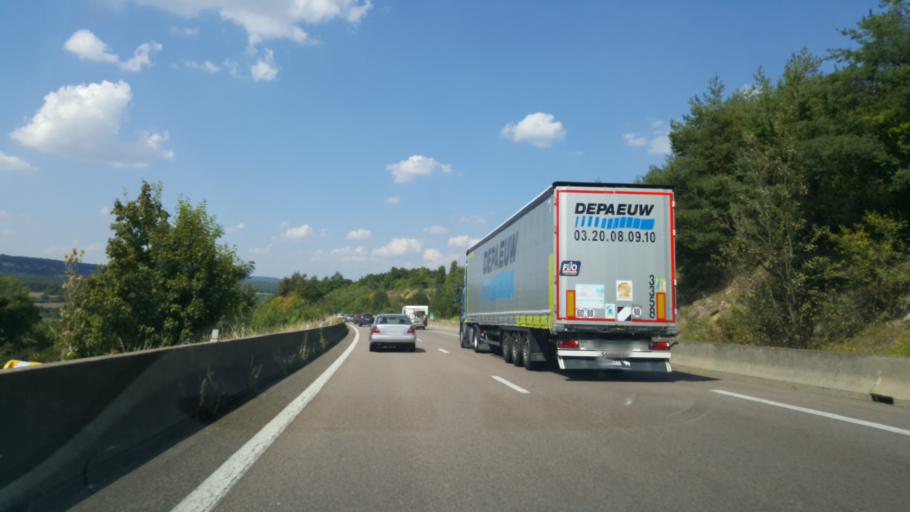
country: FR
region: Bourgogne
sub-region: Departement de la Cote-d'Or
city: Savigny-les-Beaune
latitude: 47.1450
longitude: 4.7015
